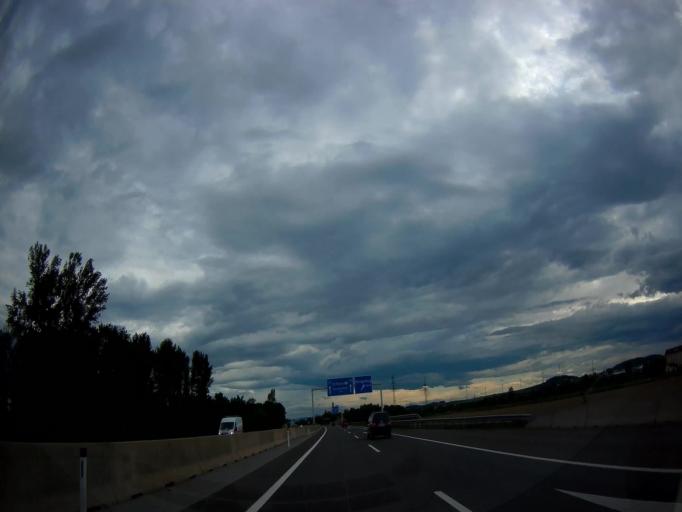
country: AT
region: Lower Austria
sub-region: Politischer Bezirk Sankt Polten
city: Herzogenburg
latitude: 48.3012
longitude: 15.7076
